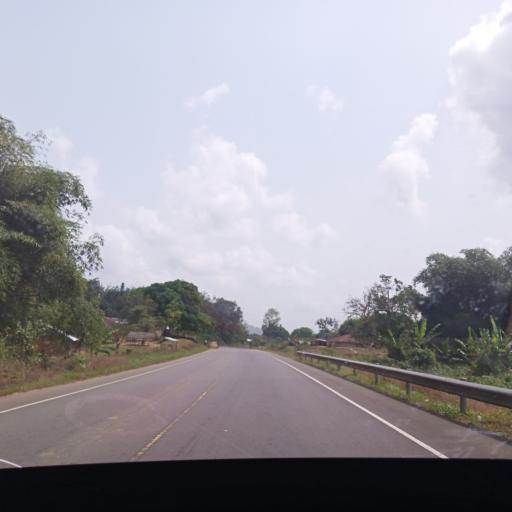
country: LR
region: Margibi
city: Kakata
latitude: 6.2507
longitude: -10.2979
